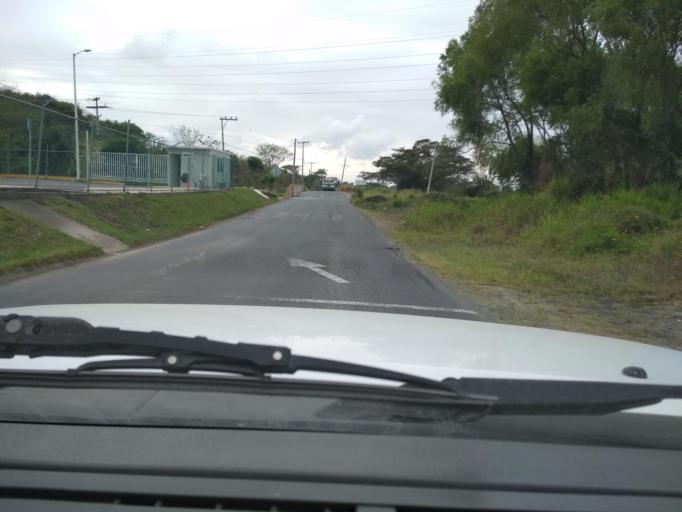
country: MX
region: Veracruz
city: Boca del Rio
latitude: 19.0899
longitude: -96.1226
